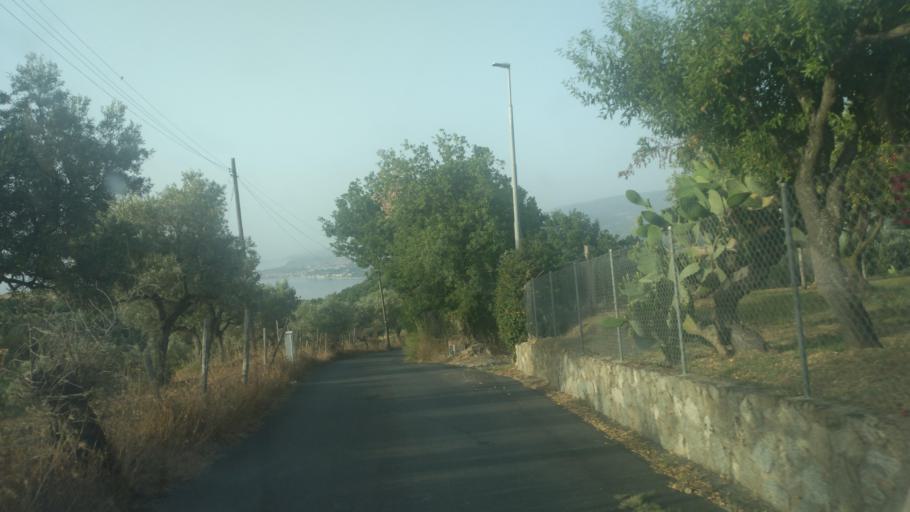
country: IT
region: Calabria
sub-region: Provincia di Catanzaro
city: Staletti
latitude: 38.7592
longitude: 16.5336
